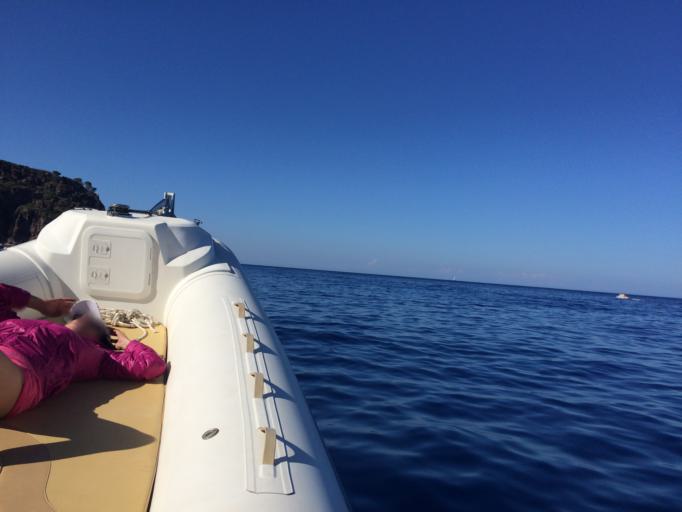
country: IT
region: Tuscany
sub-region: Provincia di Livorno
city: Capraia Isola
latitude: 43.0393
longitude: 9.8484
